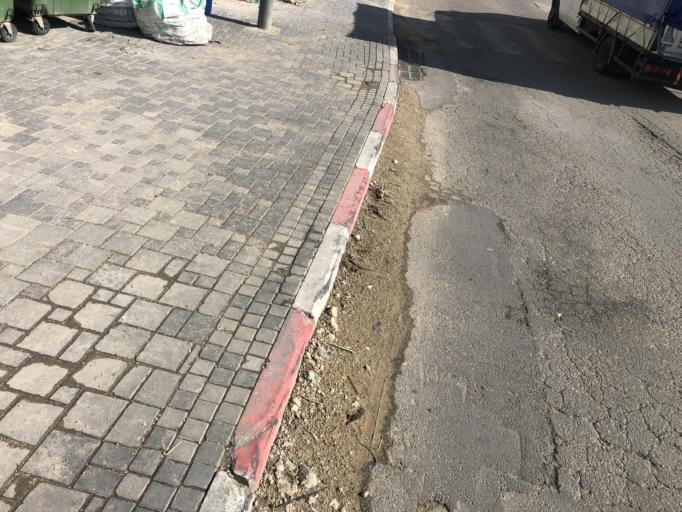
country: IL
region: Jerusalem
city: Modiin Ilit
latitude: 31.9218
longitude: 35.0533
